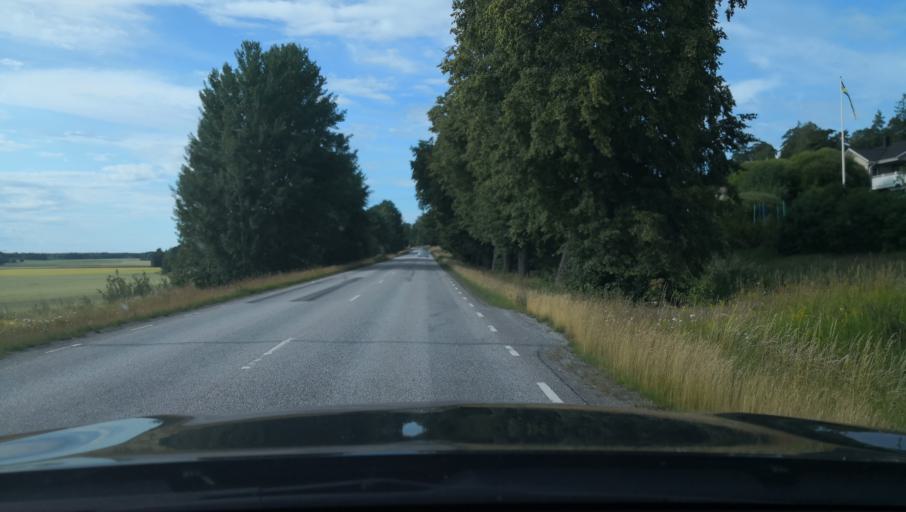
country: SE
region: Uppsala
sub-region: Habo Kommun
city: Balsta
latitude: 59.5965
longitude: 17.5100
